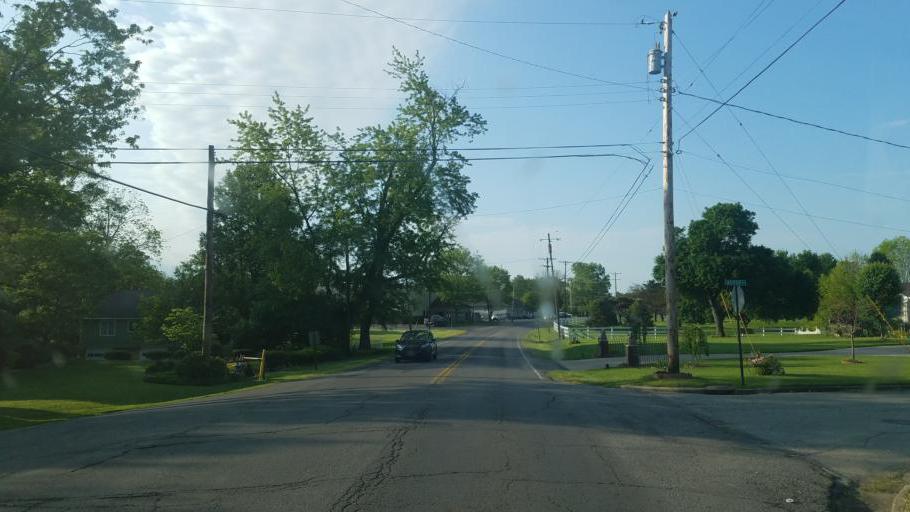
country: US
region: Ohio
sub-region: Fayette County
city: Washington Court House
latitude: 39.5318
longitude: -83.4439
